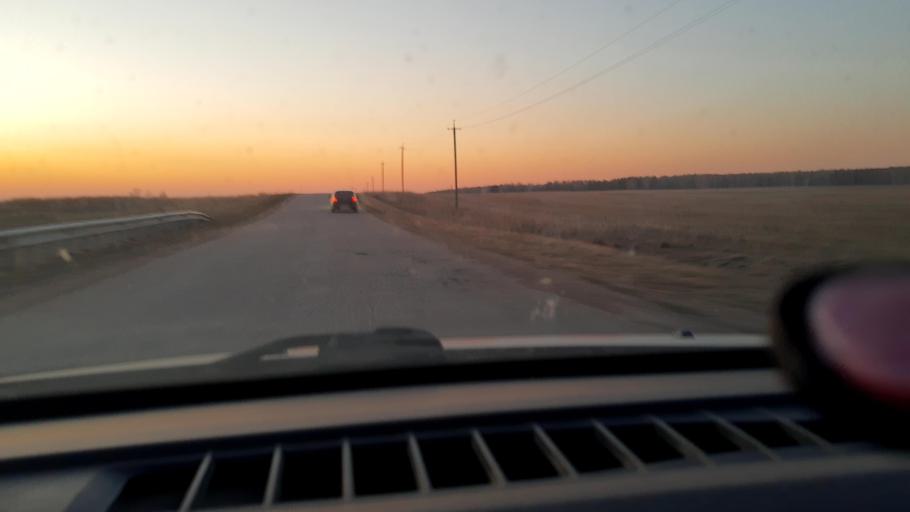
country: RU
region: Bashkortostan
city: Asanovo
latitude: 54.8114
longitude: 55.4823
